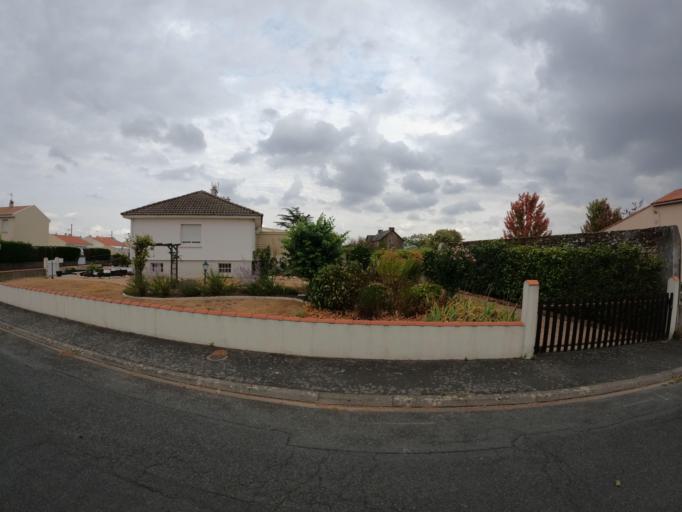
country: FR
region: Pays de la Loire
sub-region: Departement de Maine-et-Loire
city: Le Longeron
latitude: 47.0197
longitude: -1.0586
